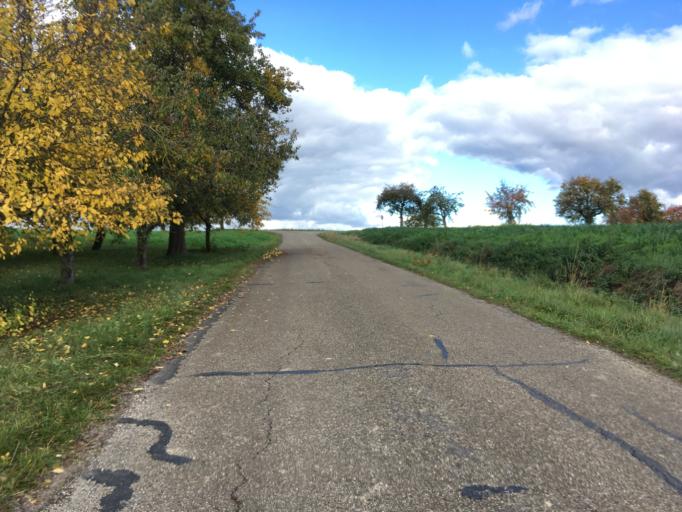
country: DE
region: Baden-Wuerttemberg
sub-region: Regierungsbezirk Stuttgart
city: Untermunkheim
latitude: 49.1849
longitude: 9.7099
